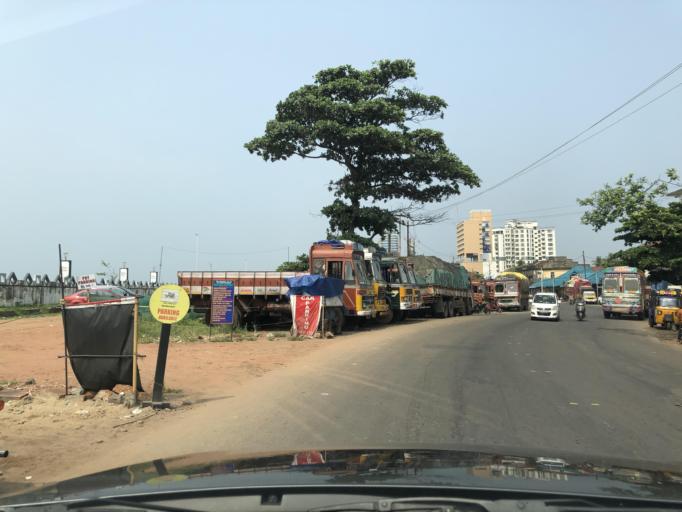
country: IN
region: Kerala
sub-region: Kozhikode
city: Kozhikode
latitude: 11.2480
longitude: 75.7726
